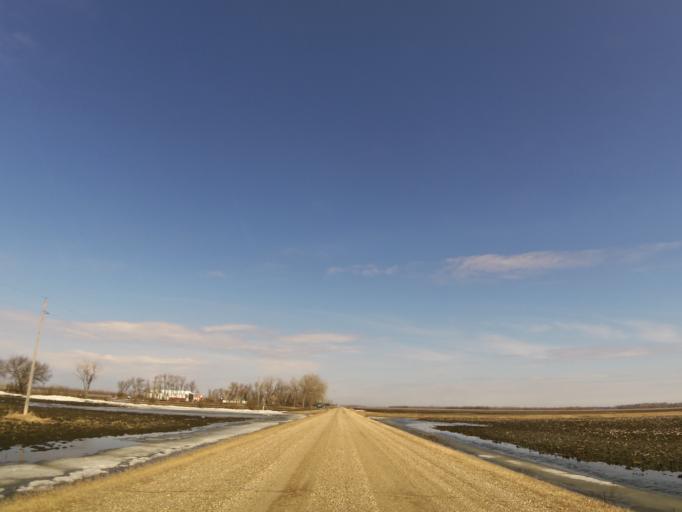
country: US
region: North Dakota
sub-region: Walsh County
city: Grafton
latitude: 48.4036
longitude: -97.1685
